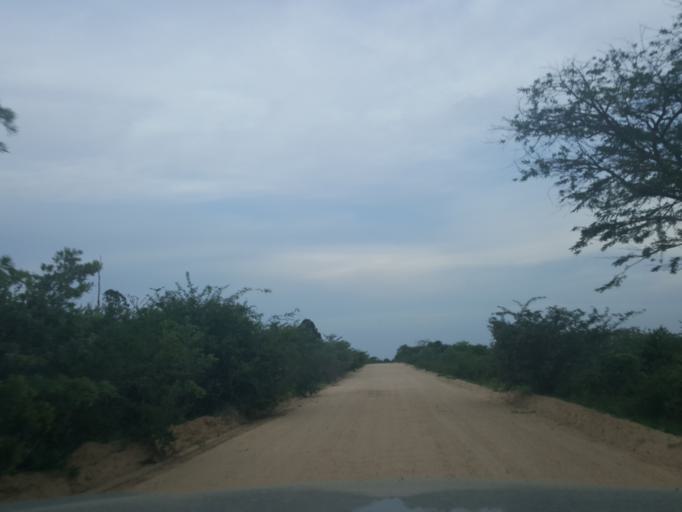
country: ZA
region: Limpopo
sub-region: Mopani District Municipality
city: Hoedspruit
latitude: -24.5647
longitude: 31.0125
